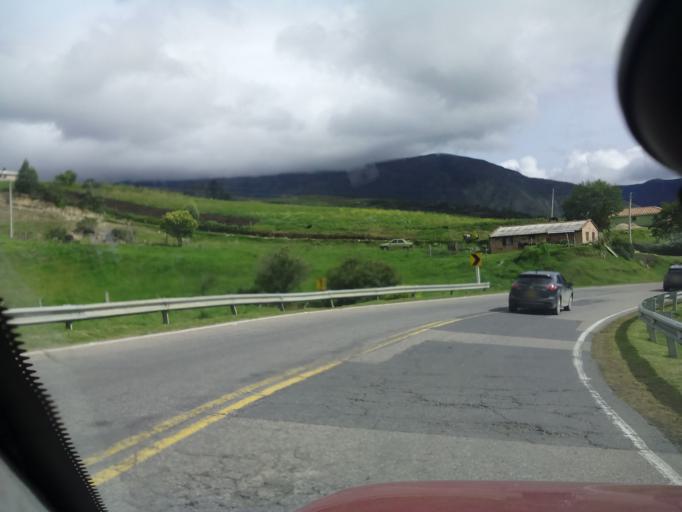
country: CO
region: Boyaca
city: Combita
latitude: 5.6863
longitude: -73.3667
